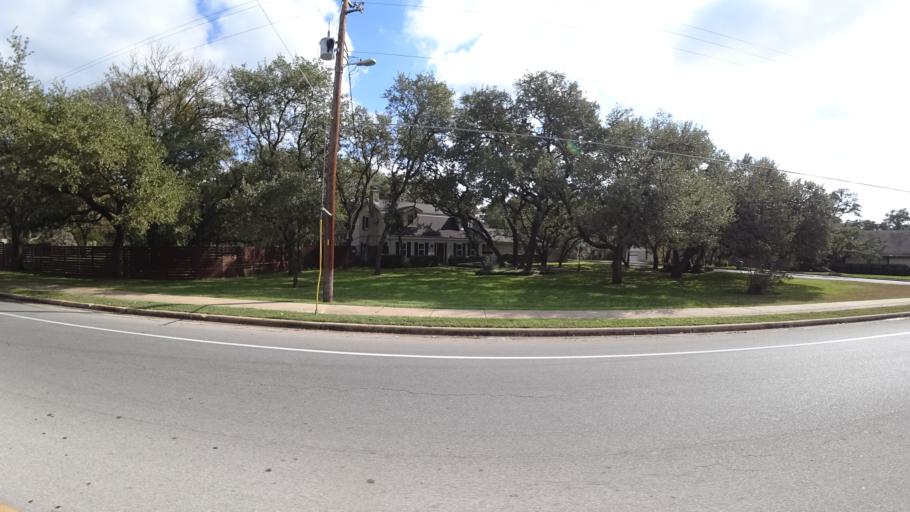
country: US
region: Texas
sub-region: Travis County
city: Shady Hollow
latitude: 30.1703
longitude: -97.8590
